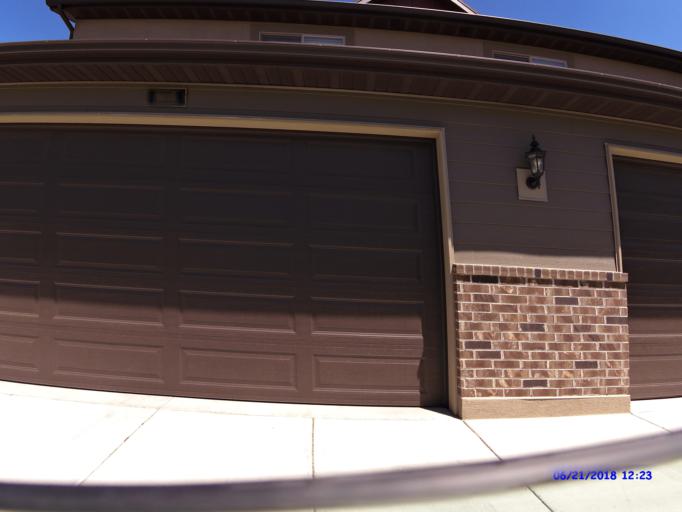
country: US
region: Utah
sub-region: Weber County
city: Harrisville
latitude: 41.2833
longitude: -111.9995
